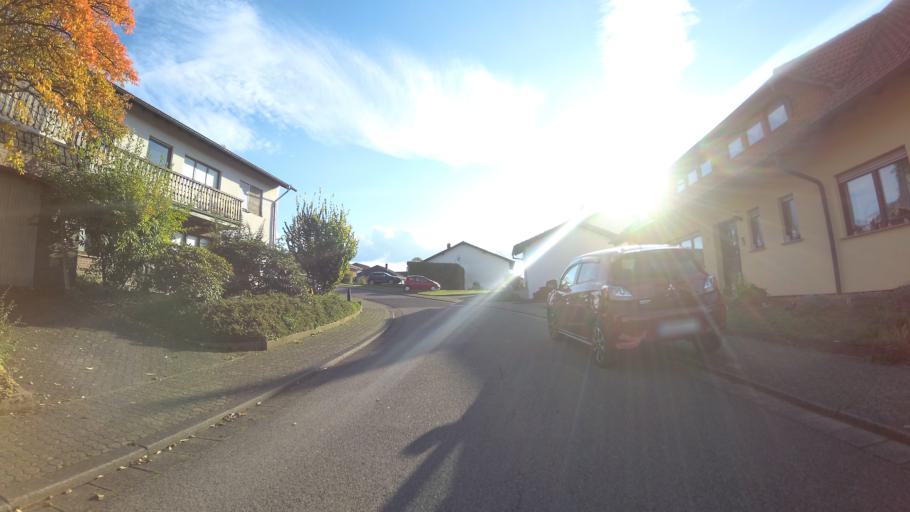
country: DE
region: Saarland
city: Marpingen
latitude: 49.4698
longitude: 7.0736
